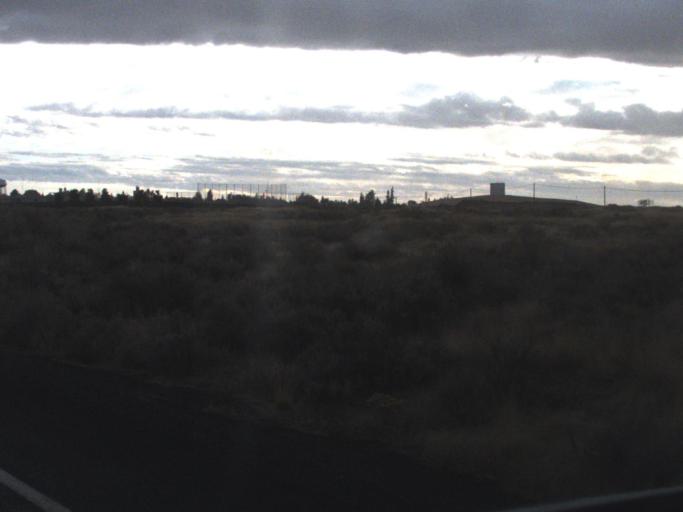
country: US
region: Washington
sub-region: Lincoln County
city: Davenport
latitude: 47.6661
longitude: -118.1410
